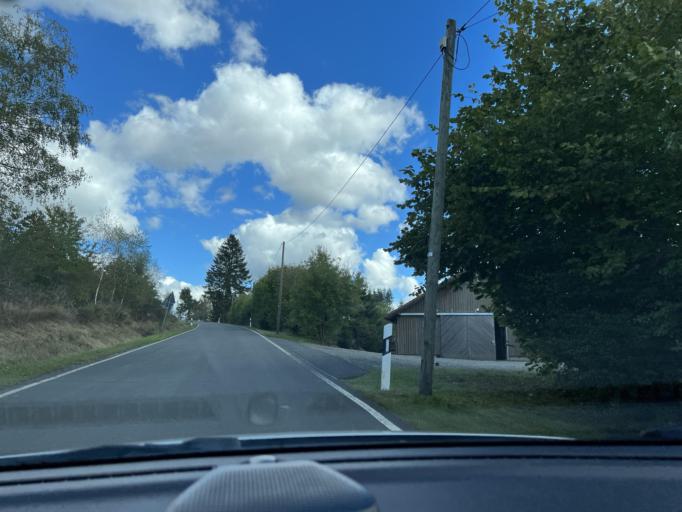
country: DE
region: North Rhine-Westphalia
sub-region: Regierungsbezirk Arnsberg
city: Bad Laasphe
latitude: 50.9716
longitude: 8.4316
